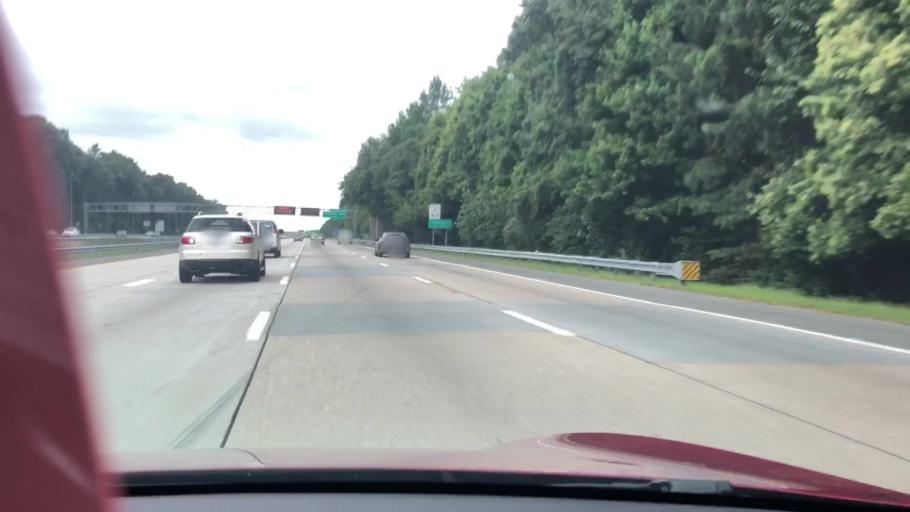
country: US
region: Virginia
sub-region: City of Chesapeake
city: Chesapeake
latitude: 36.7954
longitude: -76.2125
